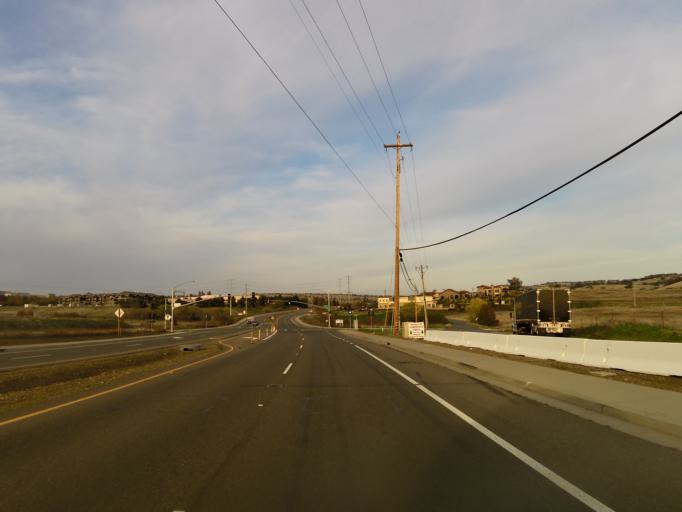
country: US
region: California
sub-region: El Dorado County
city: El Dorado Hills
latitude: 38.6431
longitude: -121.0719
